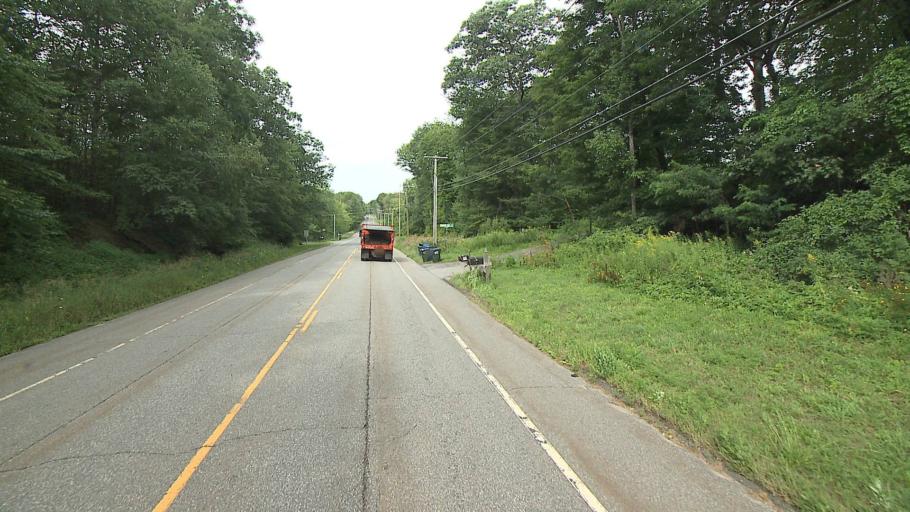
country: US
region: Connecticut
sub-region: Litchfield County
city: New Preston
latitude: 41.7434
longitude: -73.3771
